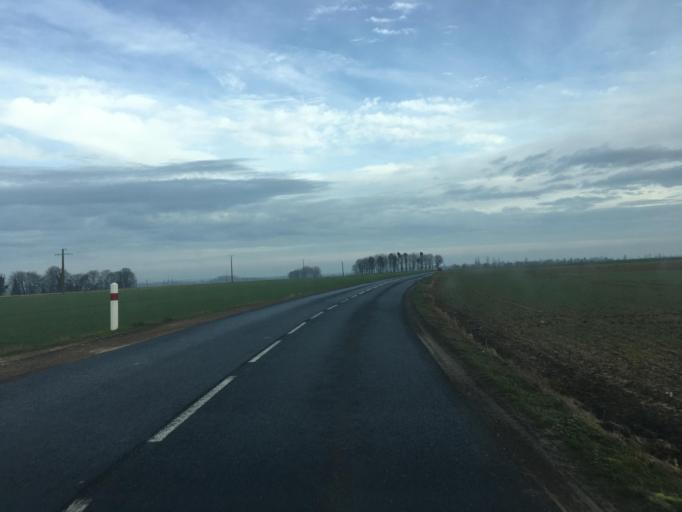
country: FR
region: Lower Normandy
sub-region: Departement du Calvados
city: Creully
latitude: 49.2374
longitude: -0.5774
